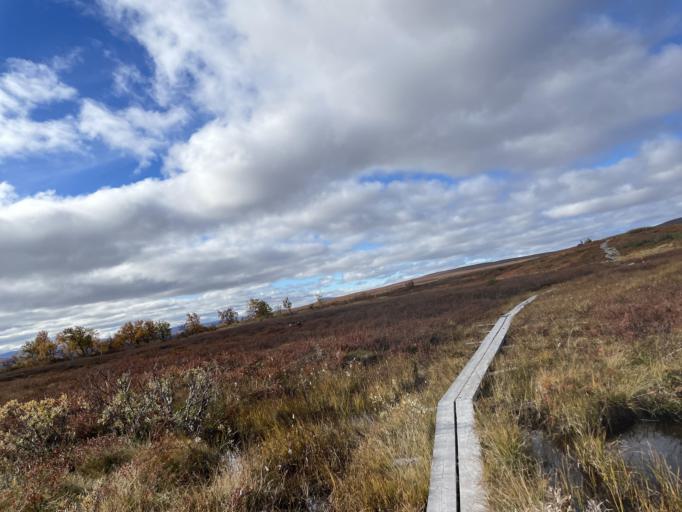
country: SE
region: Jaemtland
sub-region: Are Kommun
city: Are
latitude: 62.6946
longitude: 12.9270
